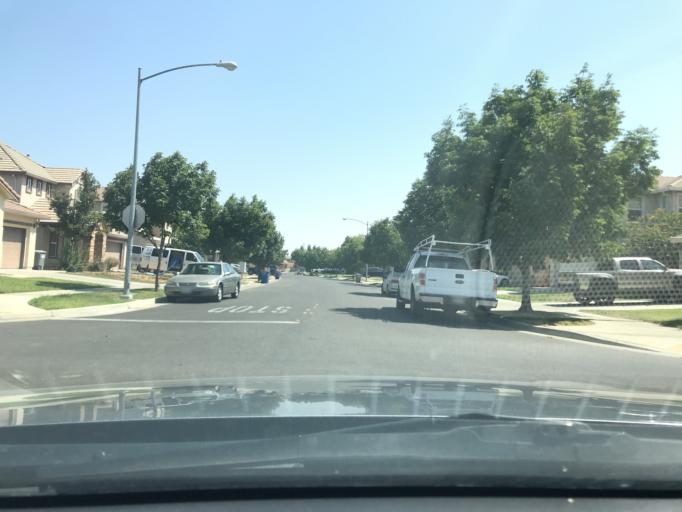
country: US
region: California
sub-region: Merced County
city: Merced
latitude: 37.3538
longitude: -120.4748
